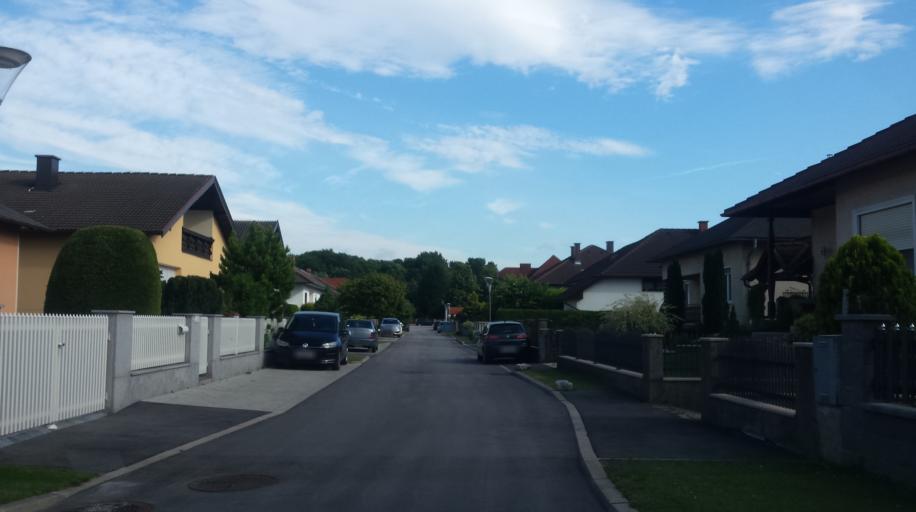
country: AT
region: Burgenland
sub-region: Eisenstadt-Umgebung
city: Leithaprodersdorf
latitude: 47.9447
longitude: 16.4807
